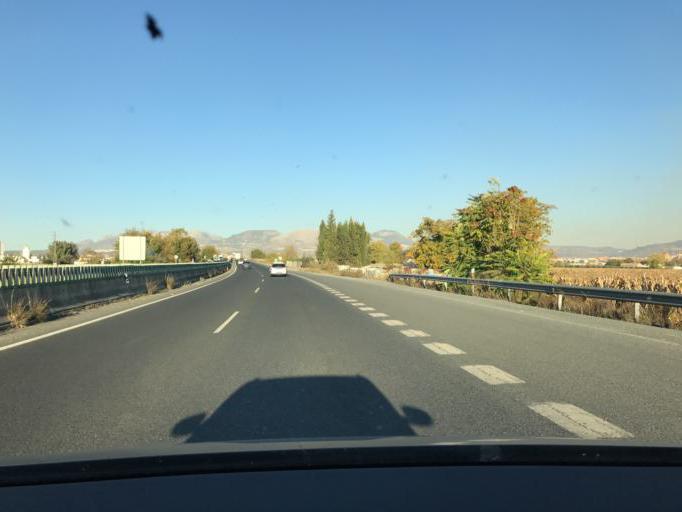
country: ES
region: Andalusia
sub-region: Provincia de Granada
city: Maracena
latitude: 37.1930
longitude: -3.6536
